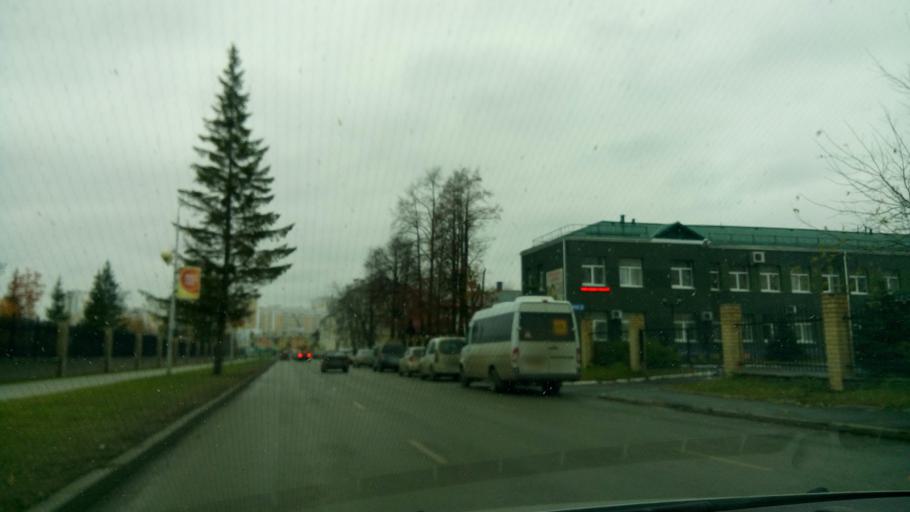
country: RU
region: Sverdlovsk
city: Verkhnyaya Pyshma
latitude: 56.9673
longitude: 60.5800
